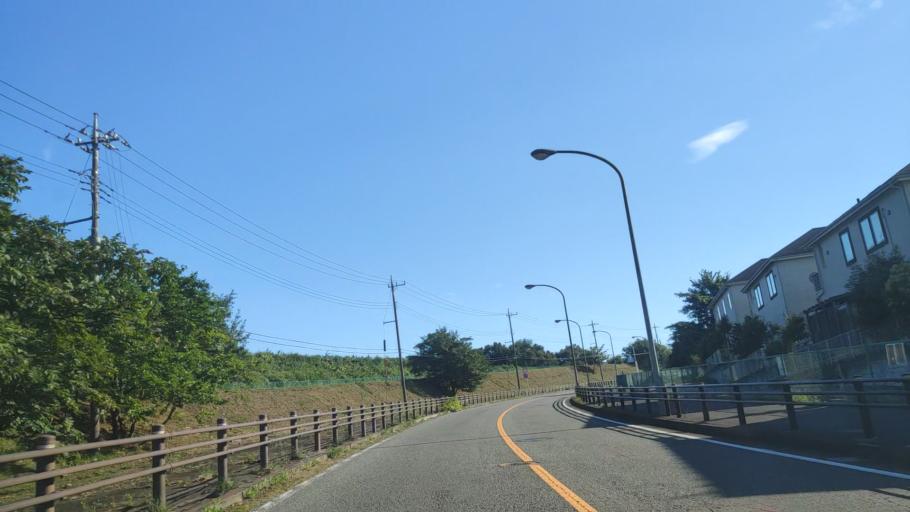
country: JP
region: Tokyo
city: Hachioji
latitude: 35.6400
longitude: 139.3318
